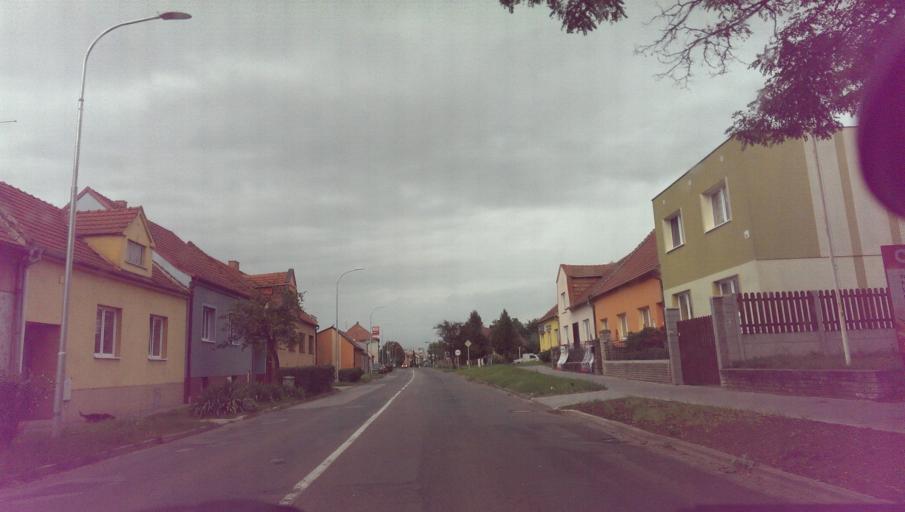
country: CZ
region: South Moravian
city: Veseli nad Moravou
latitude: 48.9580
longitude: 17.3877
